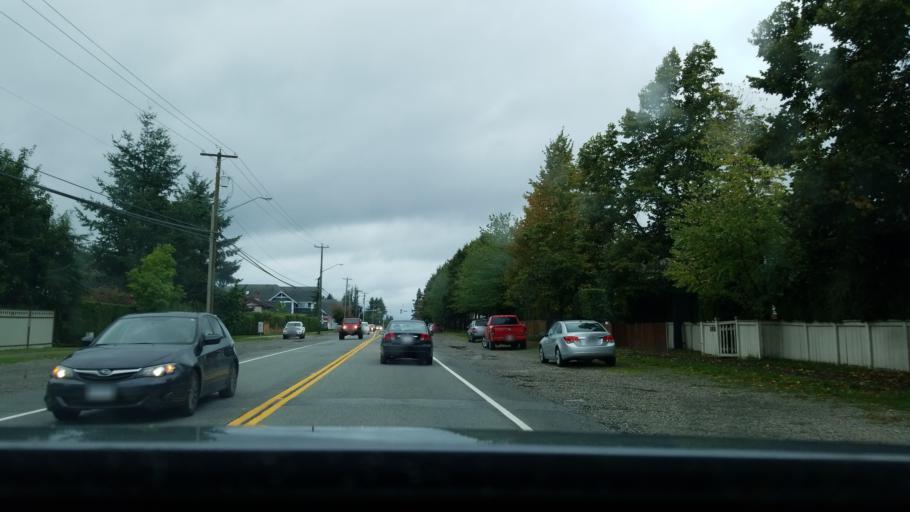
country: CA
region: British Columbia
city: Langley
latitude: 49.1188
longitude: -122.7090
